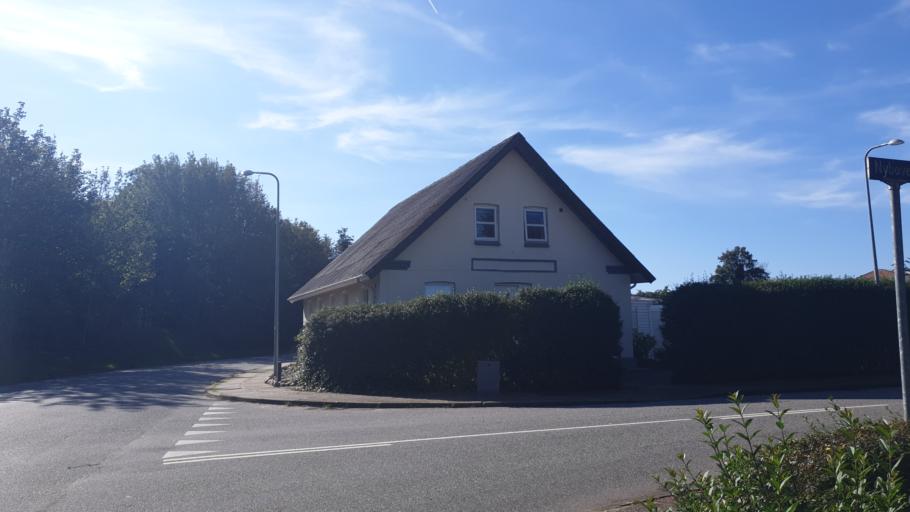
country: DK
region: Central Jutland
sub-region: Hedensted Kommune
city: Hedensted
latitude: 55.8005
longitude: 9.7004
